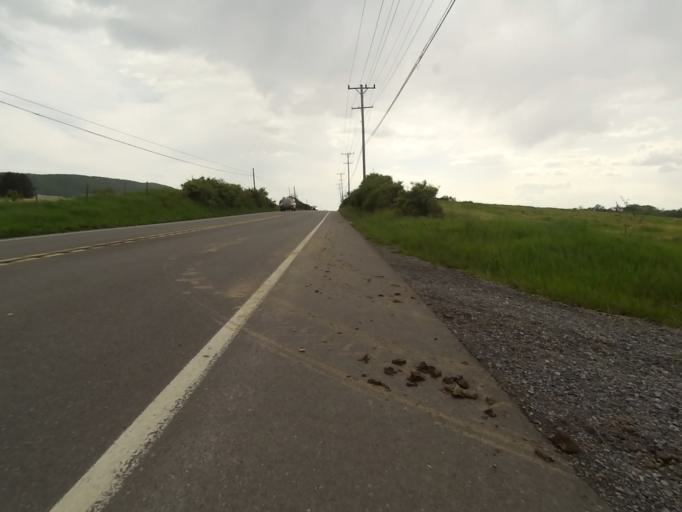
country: US
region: Pennsylvania
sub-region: Centre County
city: Zion
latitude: 40.9057
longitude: -77.6860
